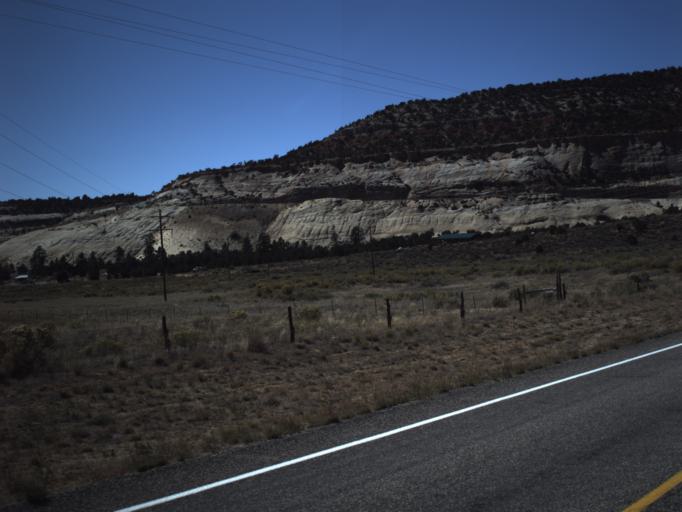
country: US
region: Utah
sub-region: Wayne County
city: Loa
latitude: 37.8980
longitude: -111.4414
